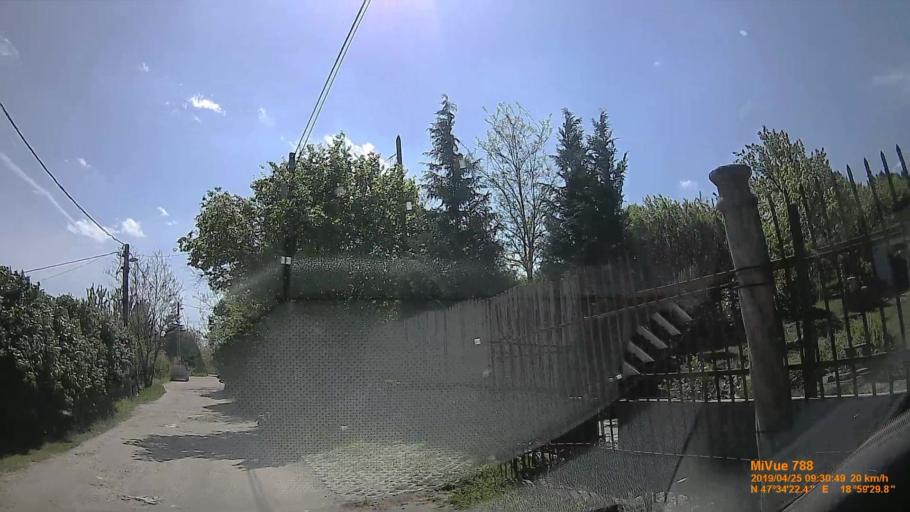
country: HU
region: Pest
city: Urom
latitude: 47.5728
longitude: 18.9917
